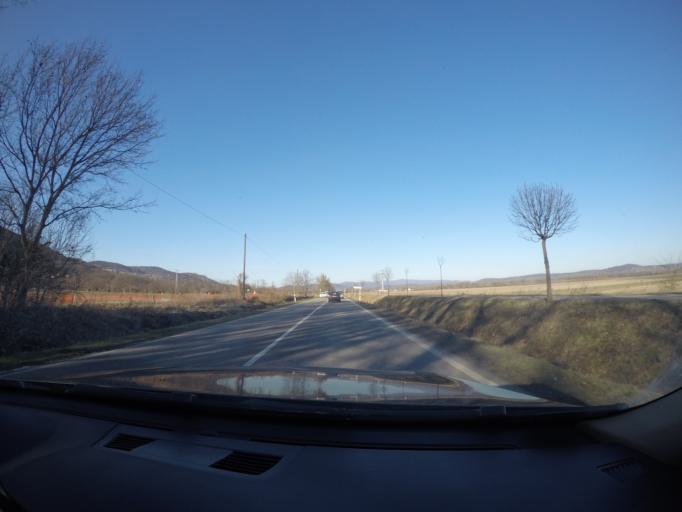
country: HU
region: Pest
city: Dunabogdany
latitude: 47.7783
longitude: 19.0528
